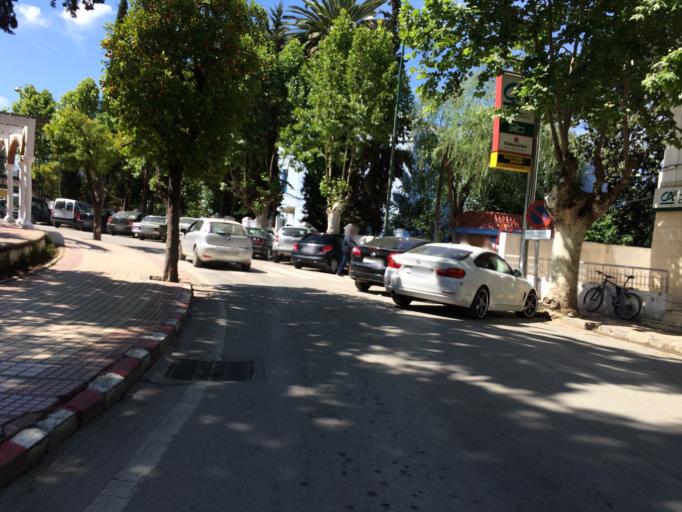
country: MA
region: Tanger-Tetouan
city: Chefchaouene
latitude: 35.1689
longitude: -5.2687
